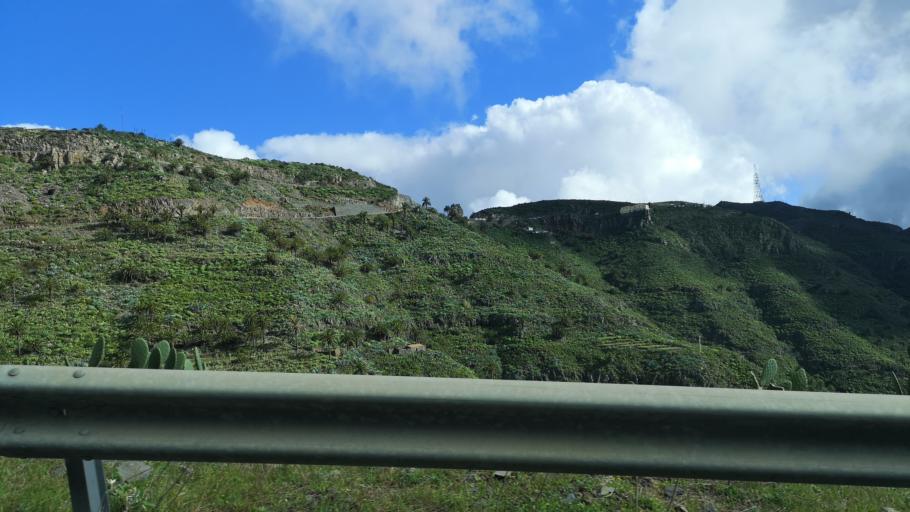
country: ES
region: Canary Islands
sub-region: Provincia de Santa Cruz de Tenerife
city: Alajero
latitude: 28.0951
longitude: -17.1902
